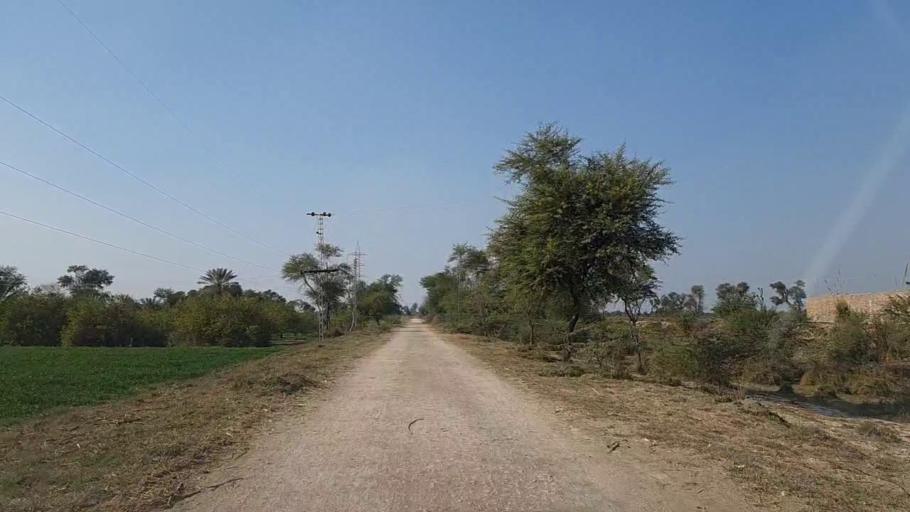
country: PK
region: Sindh
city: Daur
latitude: 26.3819
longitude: 68.3292
